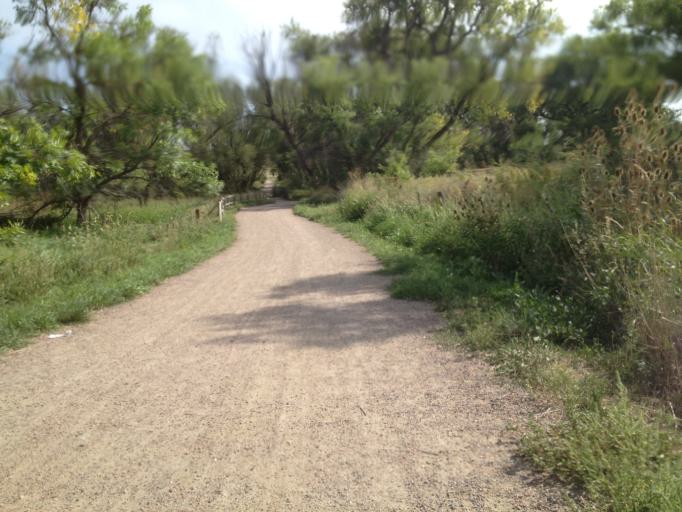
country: US
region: Colorado
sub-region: Boulder County
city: Louisville
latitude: 39.9783
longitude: -105.1138
